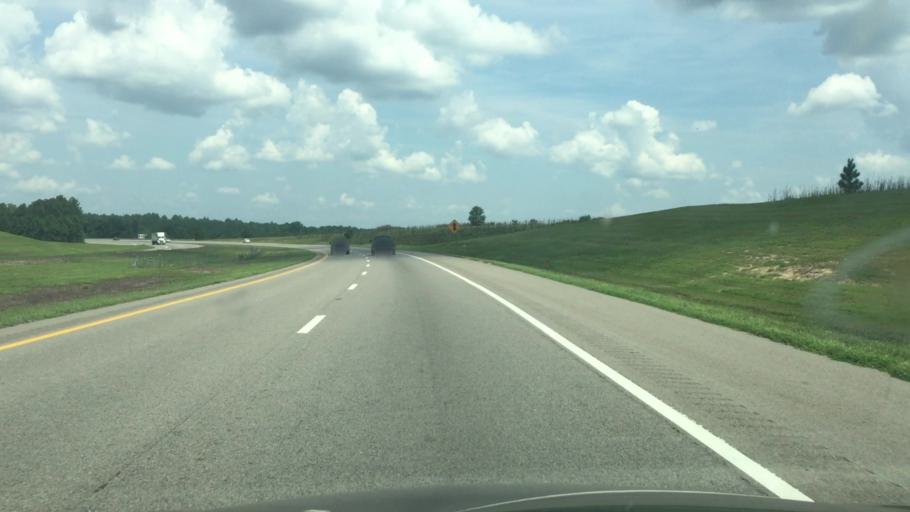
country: US
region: North Carolina
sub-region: Richmond County
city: Ellerbe
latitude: 35.1740
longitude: -79.7133
